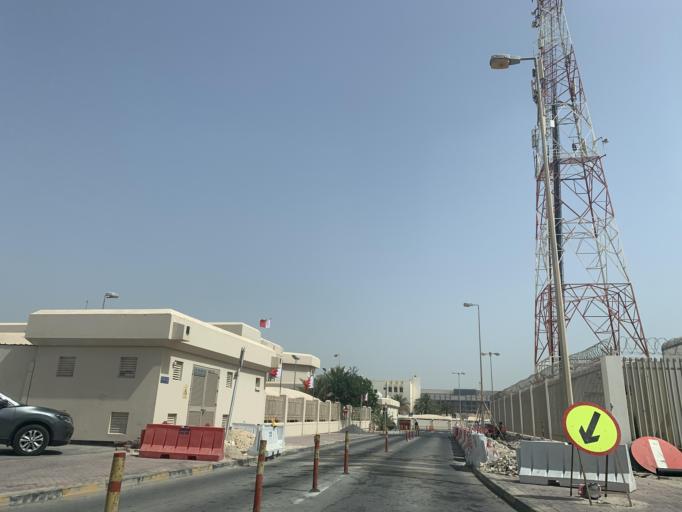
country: BH
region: Northern
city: Madinat `Isa
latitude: 26.1521
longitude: 50.5264
